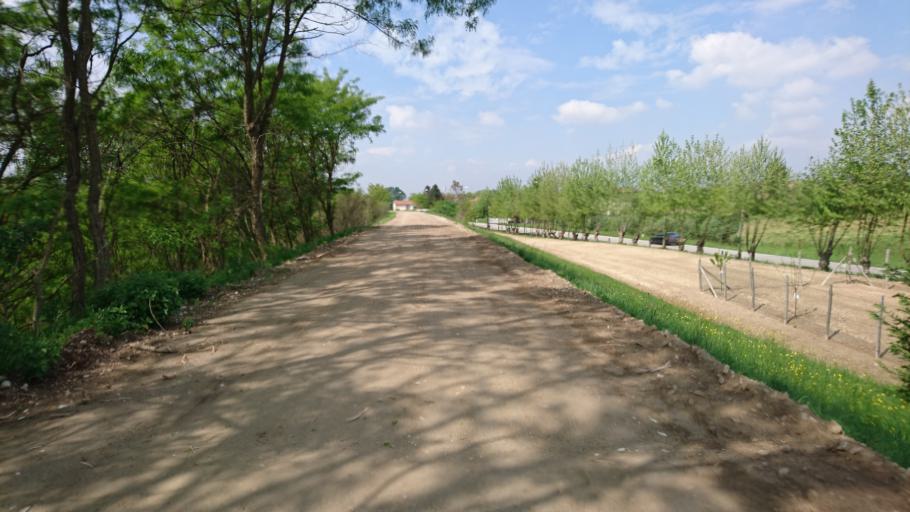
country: IT
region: Veneto
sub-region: Provincia di Padova
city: Cadoneghe
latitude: 45.4373
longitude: 11.9375
